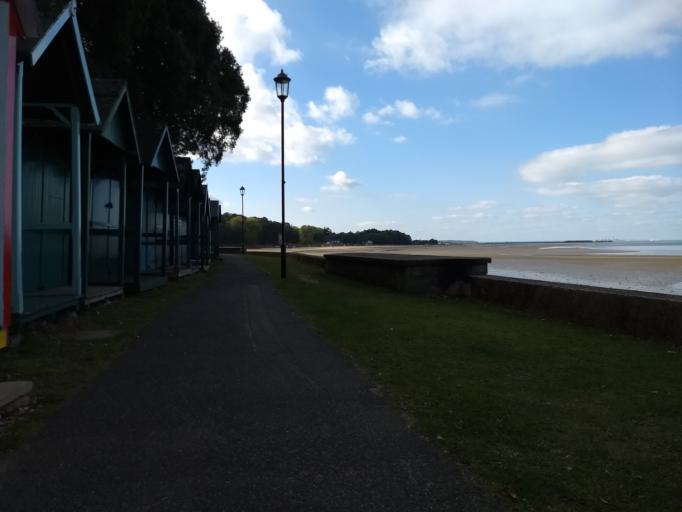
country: GB
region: England
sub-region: Isle of Wight
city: Seaview
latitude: 50.7268
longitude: -1.1318
